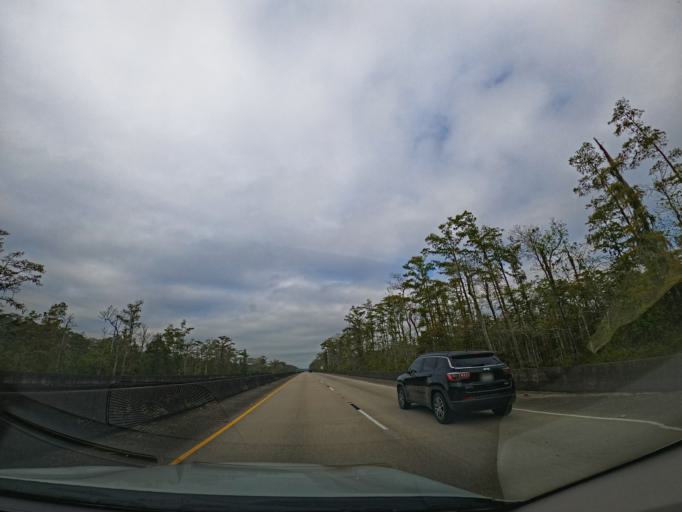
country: US
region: Louisiana
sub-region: Saint Mary Parish
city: Amelia
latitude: 29.6681
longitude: -91.0557
